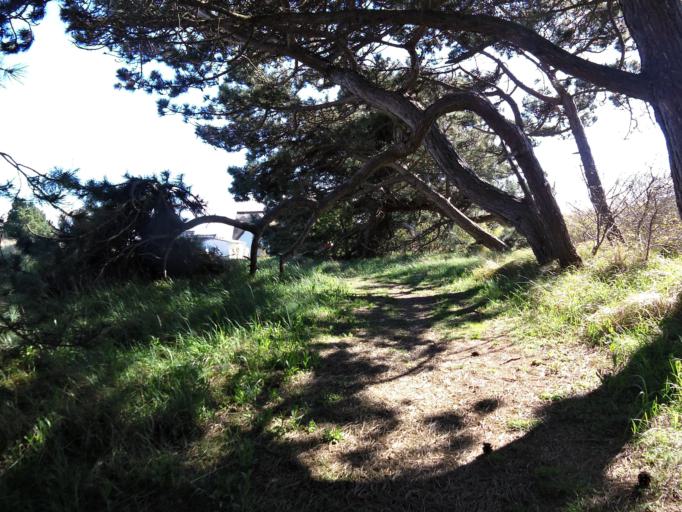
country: DE
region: Mecklenburg-Vorpommern
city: Hiddensee
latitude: 54.5274
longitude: 13.0845
